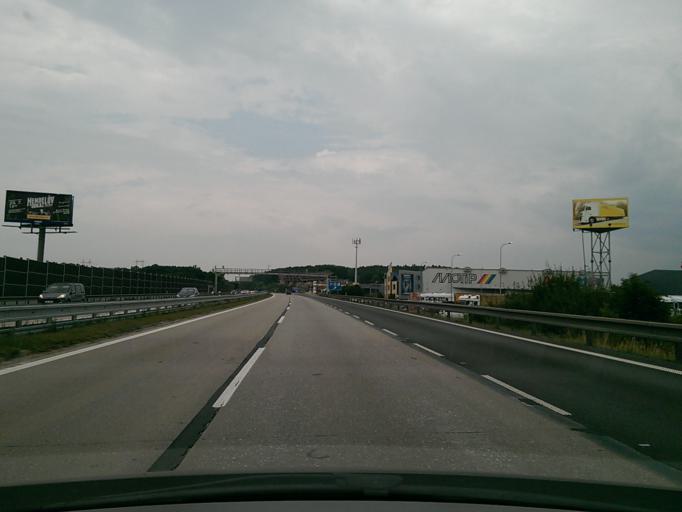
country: CZ
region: South Moravian
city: Troubsko
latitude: 49.1808
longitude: 16.4844
